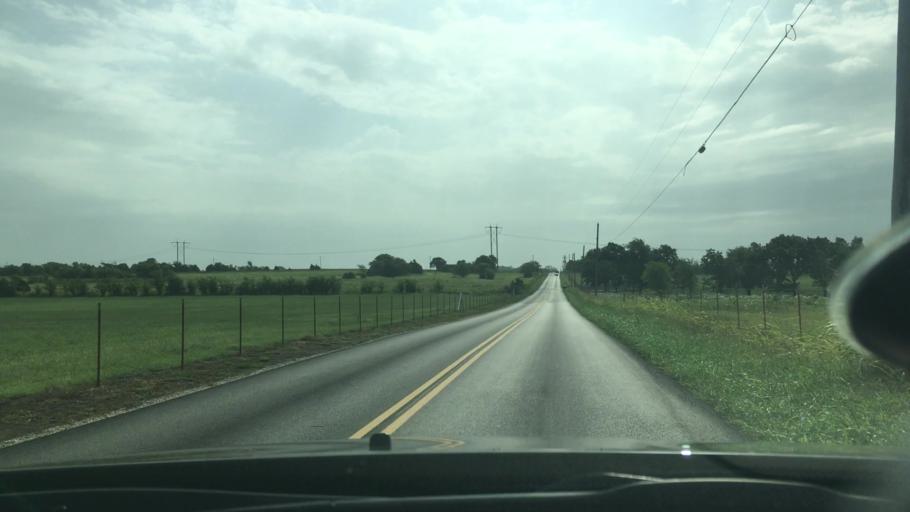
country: US
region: Oklahoma
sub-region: Carter County
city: Ardmore
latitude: 34.2020
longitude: -97.2020
